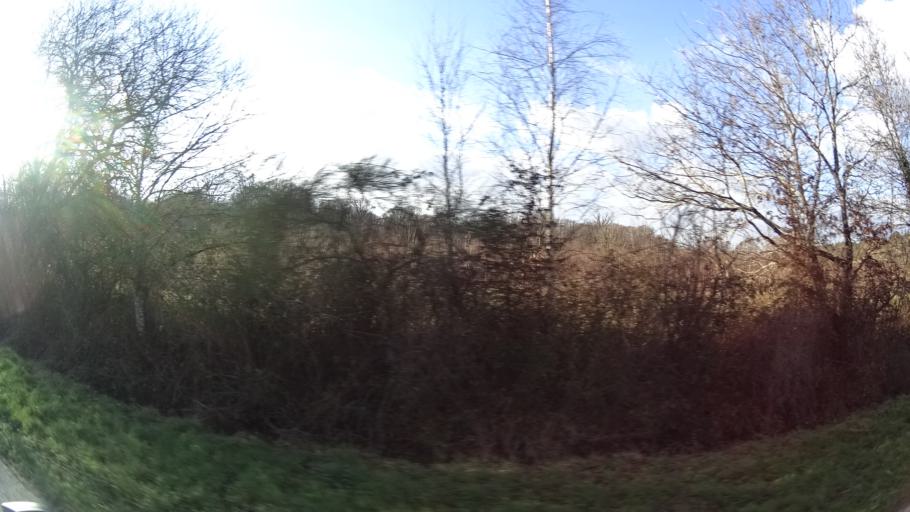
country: FR
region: Pays de la Loire
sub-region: Departement de la Loire-Atlantique
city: Plesse
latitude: 47.5595
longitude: -1.8692
